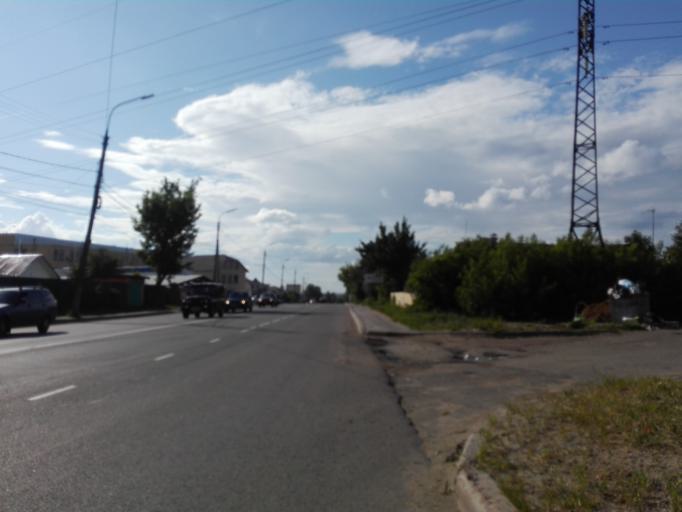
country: RU
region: Orjol
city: Orel
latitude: 52.9950
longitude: 36.1128
